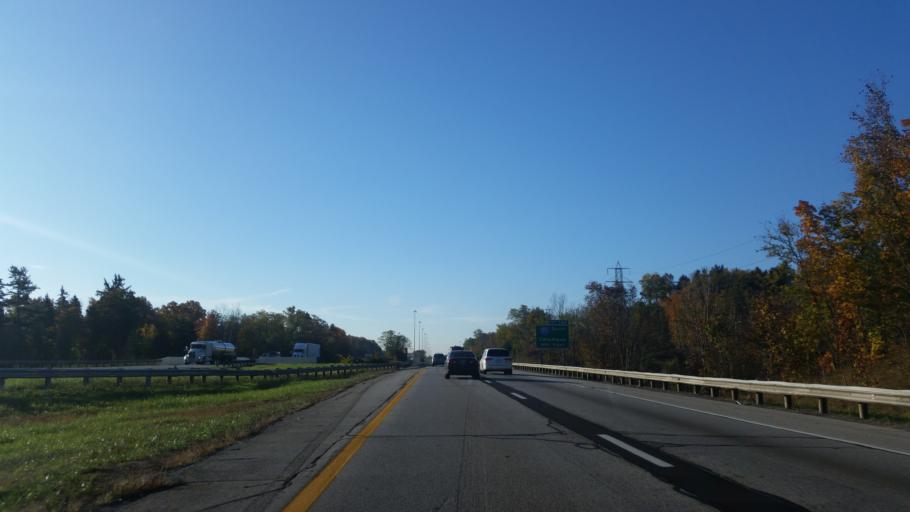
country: US
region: Ohio
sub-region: Summit County
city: Richfield
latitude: 41.2411
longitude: -81.6288
